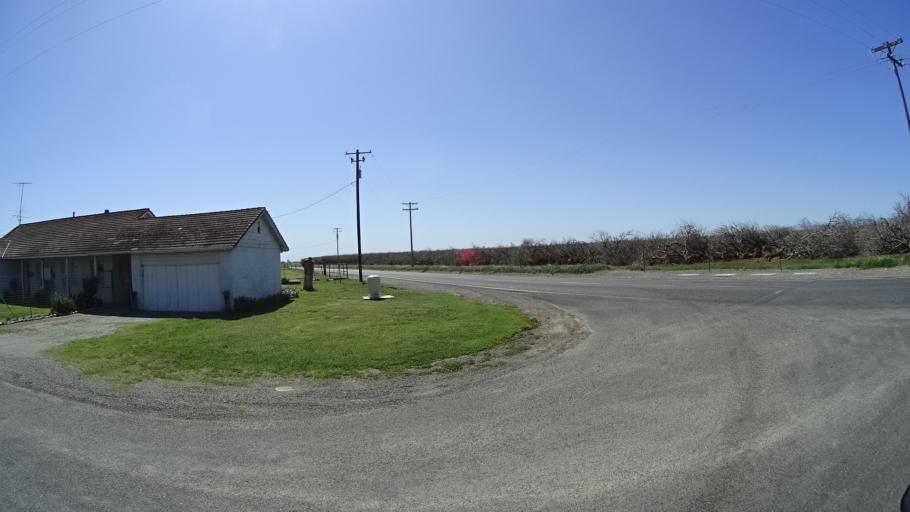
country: US
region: California
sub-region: Glenn County
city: Orland
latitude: 39.7898
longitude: -122.1207
